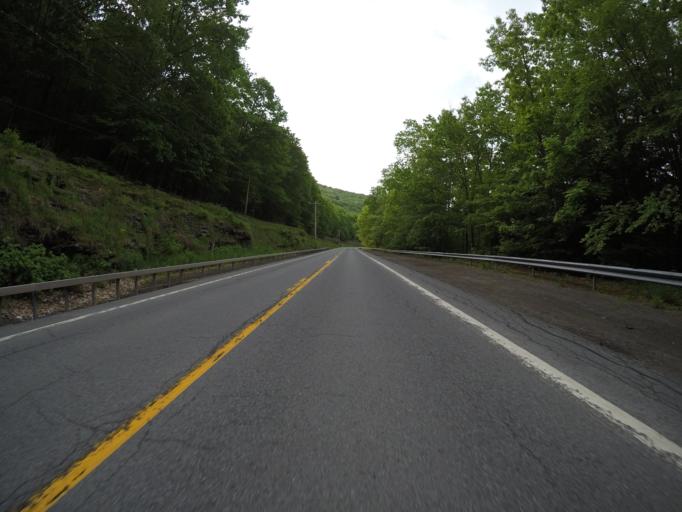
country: US
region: New York
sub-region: Sullivan County
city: Livingston Manor
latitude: 42.0858
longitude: -74.8330
